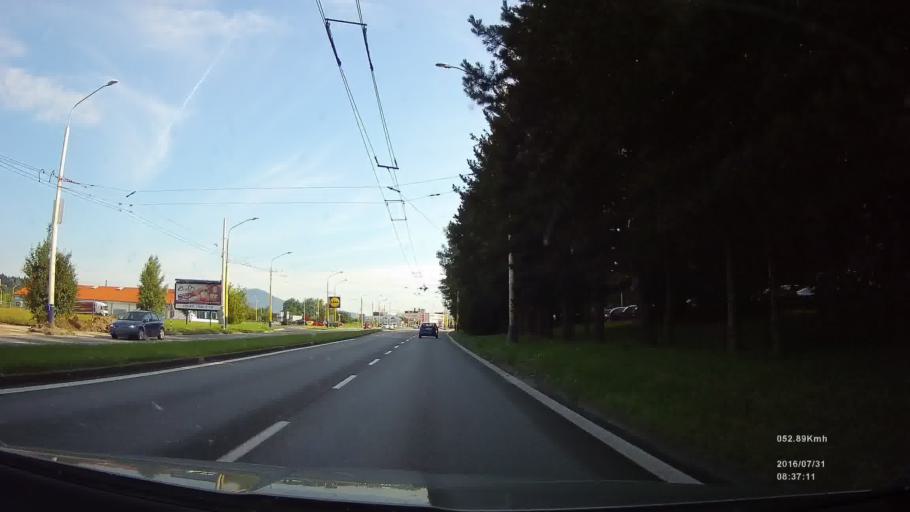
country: SK
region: Presovsky
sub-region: Okres Presov
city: Presov
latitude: 48.9888
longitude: 21.2652
